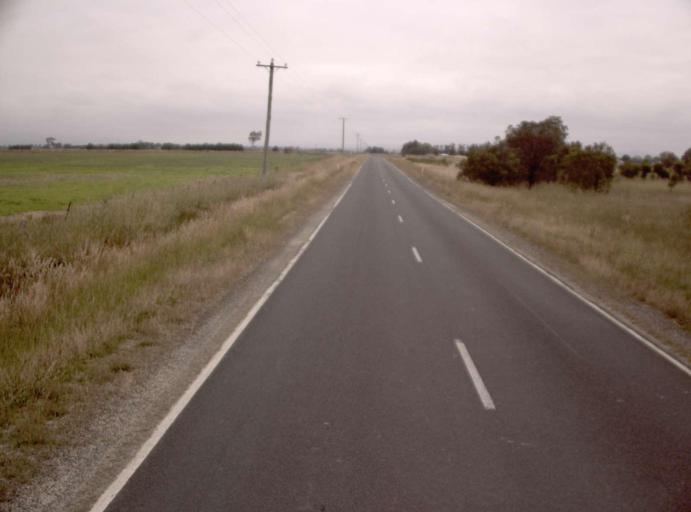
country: AU
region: Victoria
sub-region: Wellington
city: Heyfield
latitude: -38.0349
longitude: 146.7664
